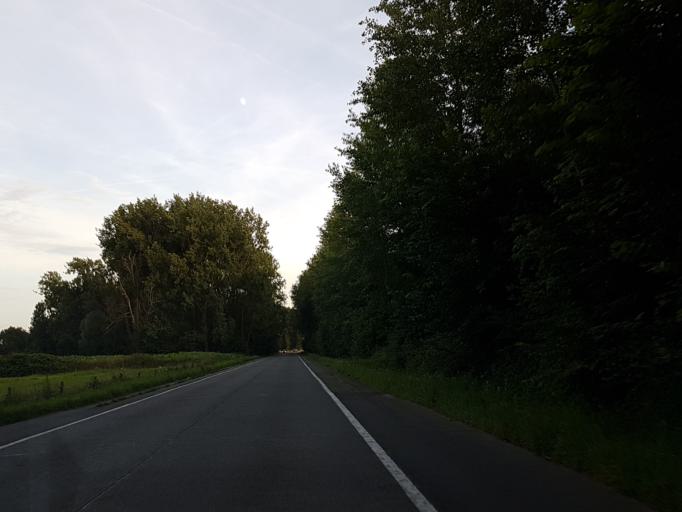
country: BE
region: Flanders
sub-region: Provincie Vlaams-Brabant
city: Londerzeel
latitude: 50.9796
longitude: 4.2702
